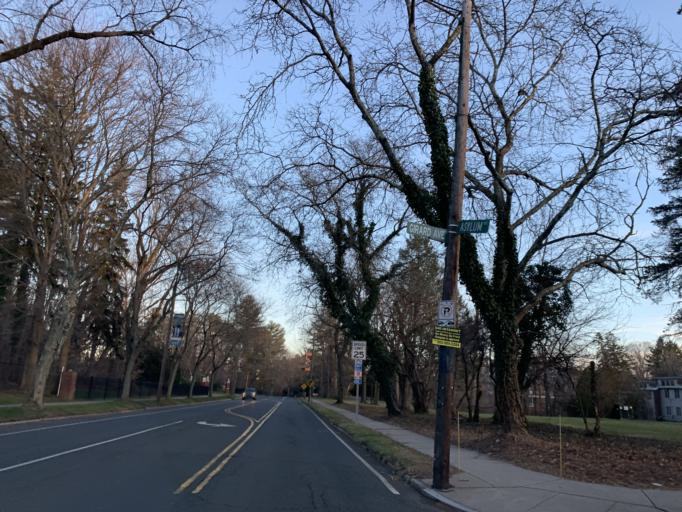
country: US
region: Connecticut
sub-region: Hartford County
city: Hartford
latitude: 41.7758
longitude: -72.7080
